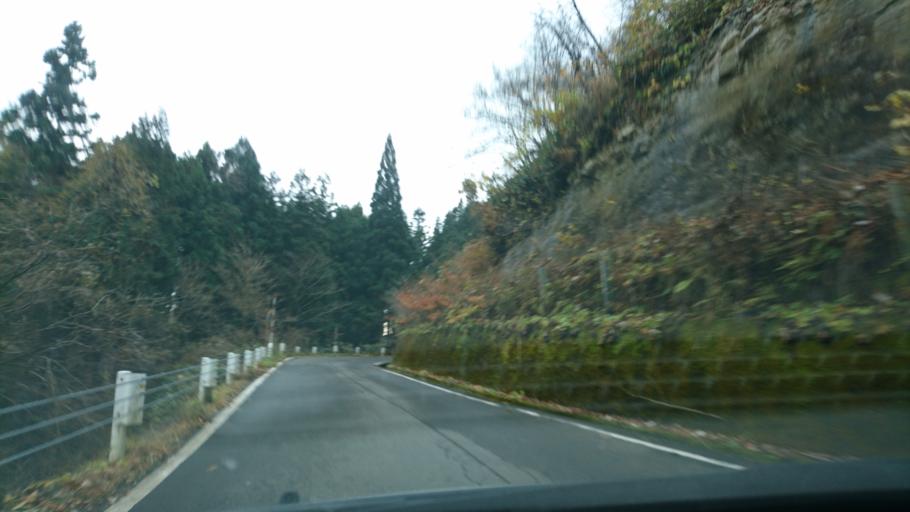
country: JP
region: Iwate
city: Ichinoseki
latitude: 38.9104
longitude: 140.9067
